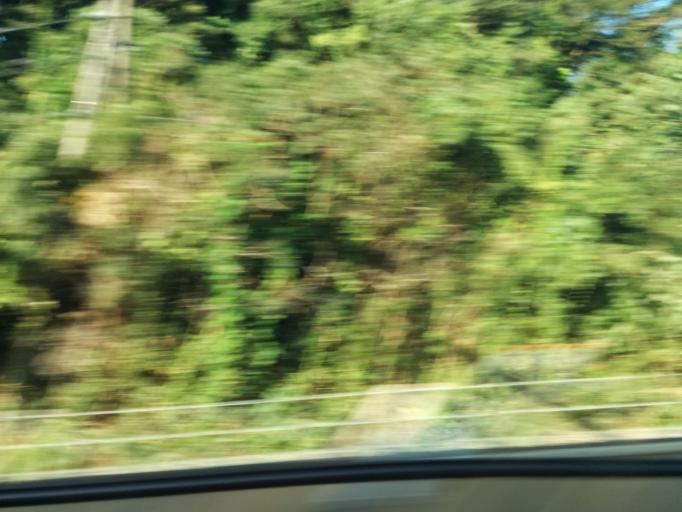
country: JP
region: Shizuoka
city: Kosai-shi
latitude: 34.7068
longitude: 137.5199
